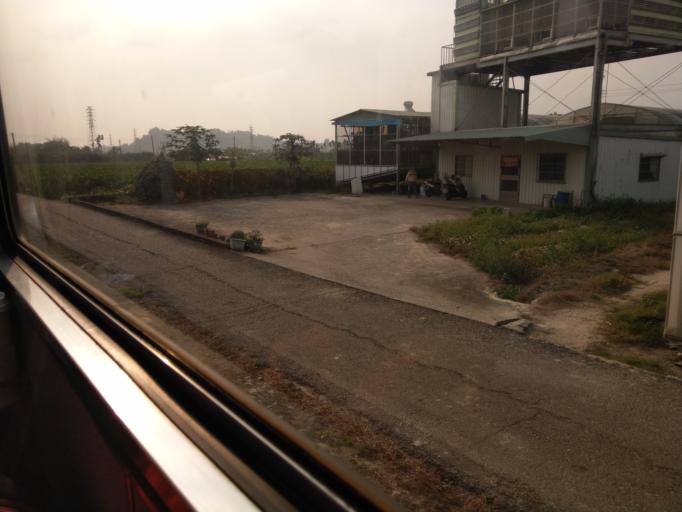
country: TW
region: Taiwan
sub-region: Chiayi
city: Jiayi Shi
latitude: 23.5085
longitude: 120.5369
